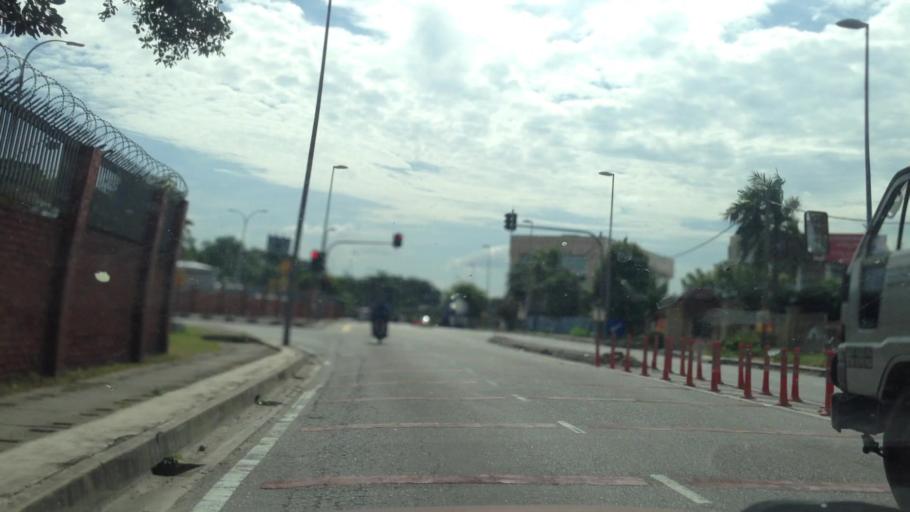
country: MY
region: Selangor
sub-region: Petaling
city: Petaling Jaya
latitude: 3.0832
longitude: 101.6218
